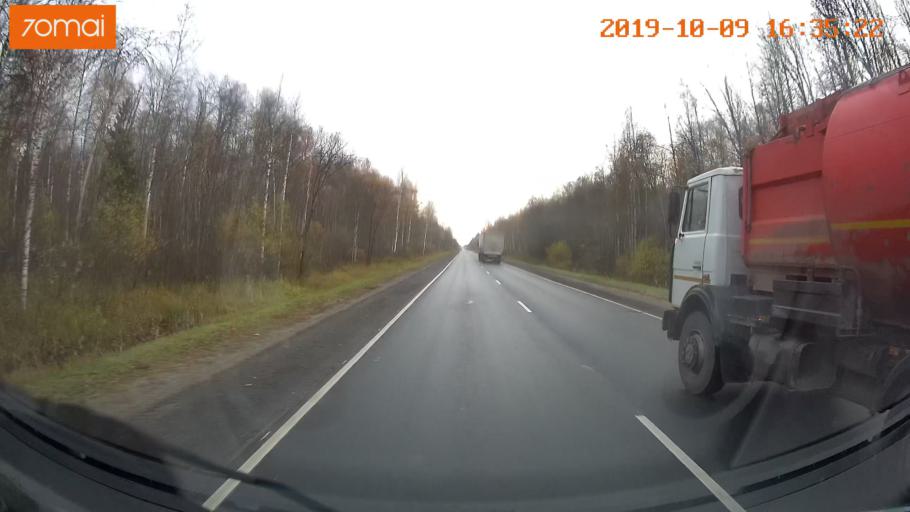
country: RU
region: Kostroma
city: Oktyabr'skiy
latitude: 57.5565
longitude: 41.0002
